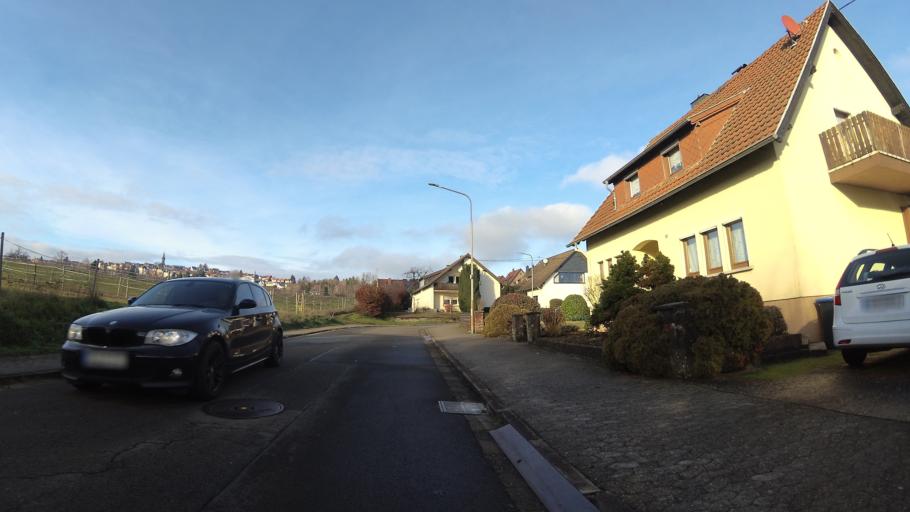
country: DE
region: Saarland
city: Spiesen-Elversberg
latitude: 49.3073
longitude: 7.1372
